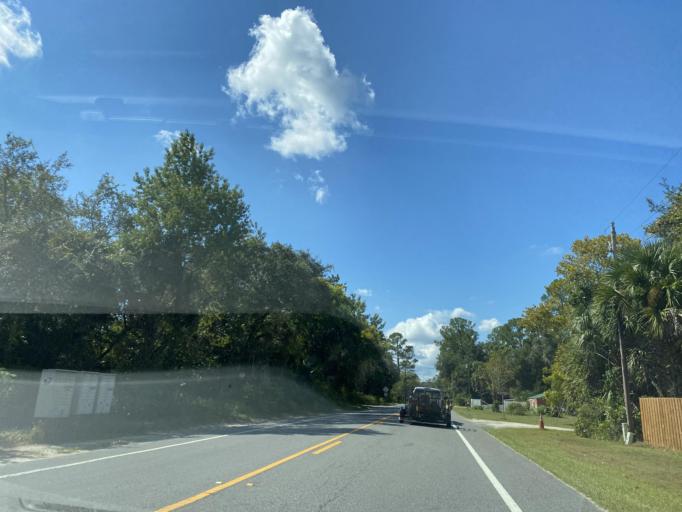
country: US
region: Florida
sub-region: Lake County
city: Lake Mack-Forest Hills
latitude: 29.0171
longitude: -81.4908
